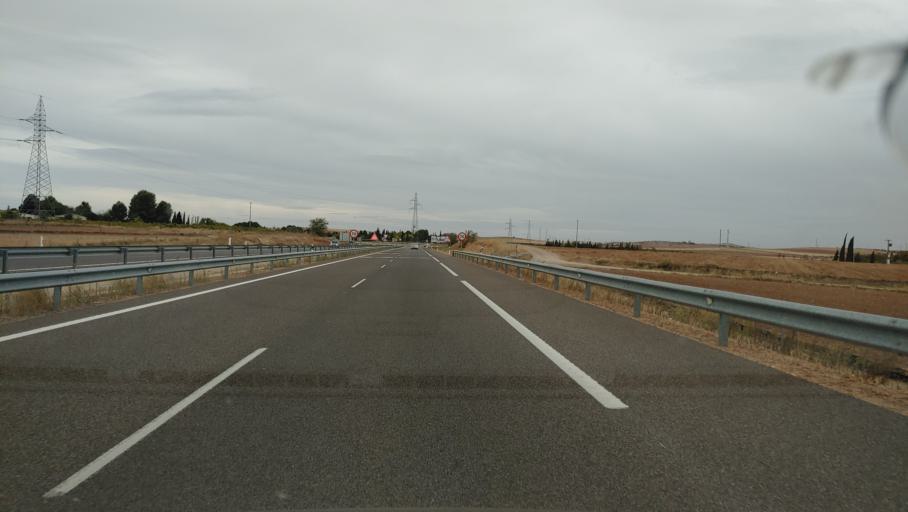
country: ES
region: Castille-La Mancha
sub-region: Provincia de Ciudad Real
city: Miguelturra
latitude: 38.9476
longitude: -3.9116
